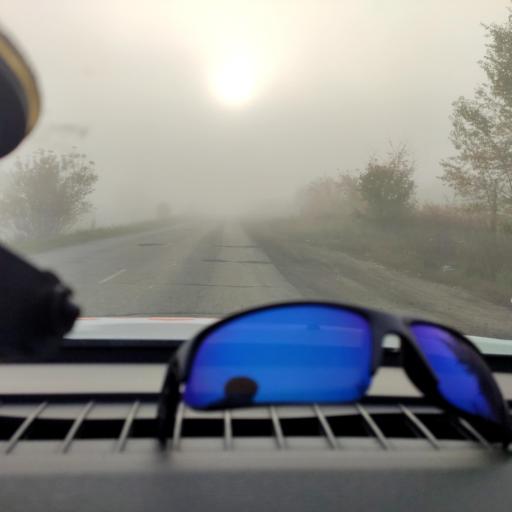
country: RU
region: Samara
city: Chapayevsk
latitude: 53.0051
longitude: 49.7449
